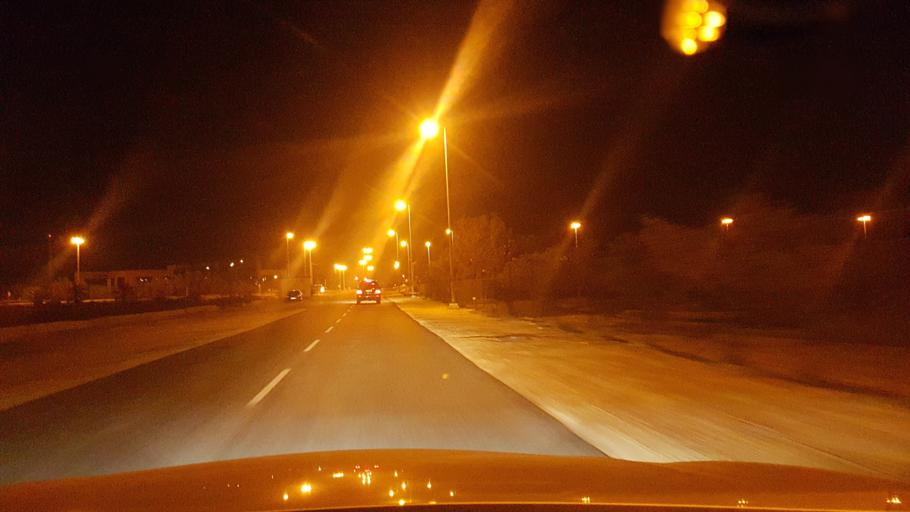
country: BH
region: Central Governorate
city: Dar Kulayb
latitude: 26.0179
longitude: 50.4851
